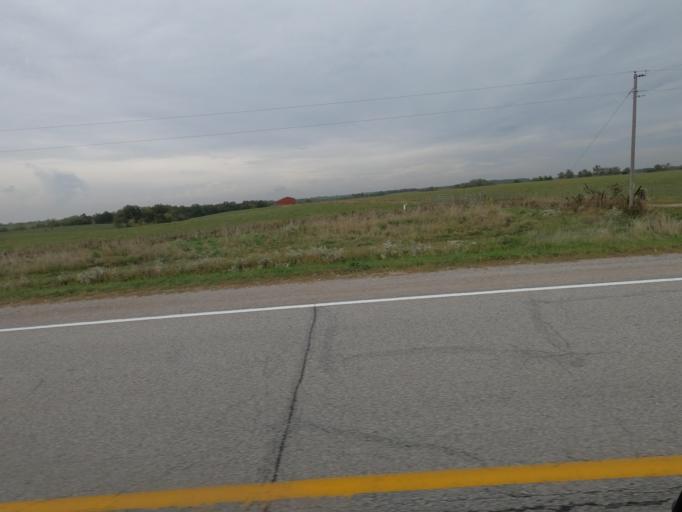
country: US
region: Iowa
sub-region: Van Buren County
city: Keosauqua
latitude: 40.8564
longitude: -92.0642
